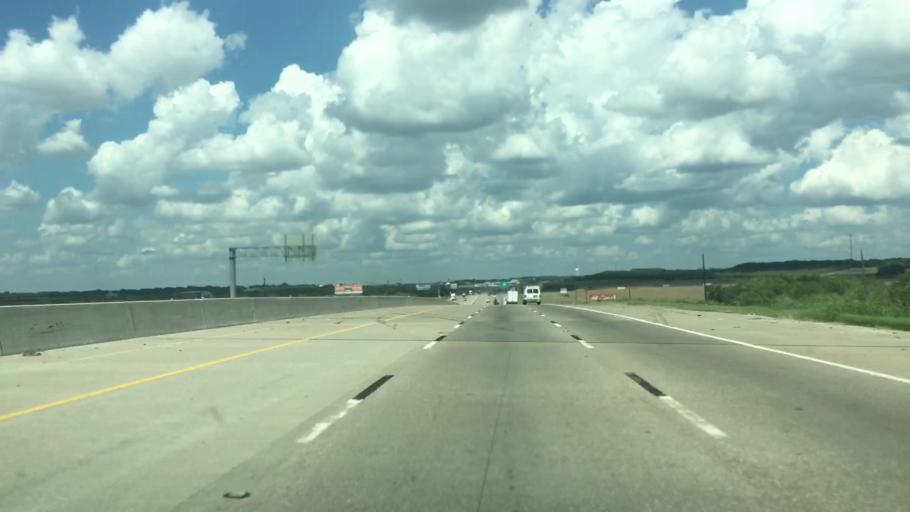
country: US
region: Texas
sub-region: Hill County
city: Hillsboro
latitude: 31.9833
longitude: -97.1094
